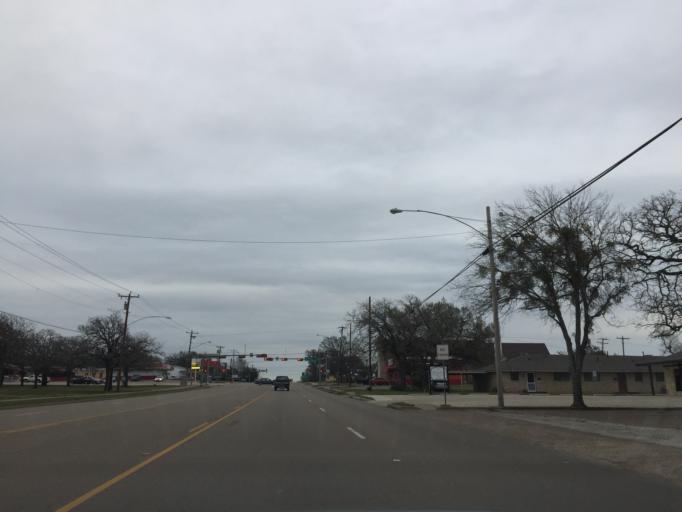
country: US
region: Texas
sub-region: Coryell County
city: Gatesville
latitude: 31.4346
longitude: -97.7228
